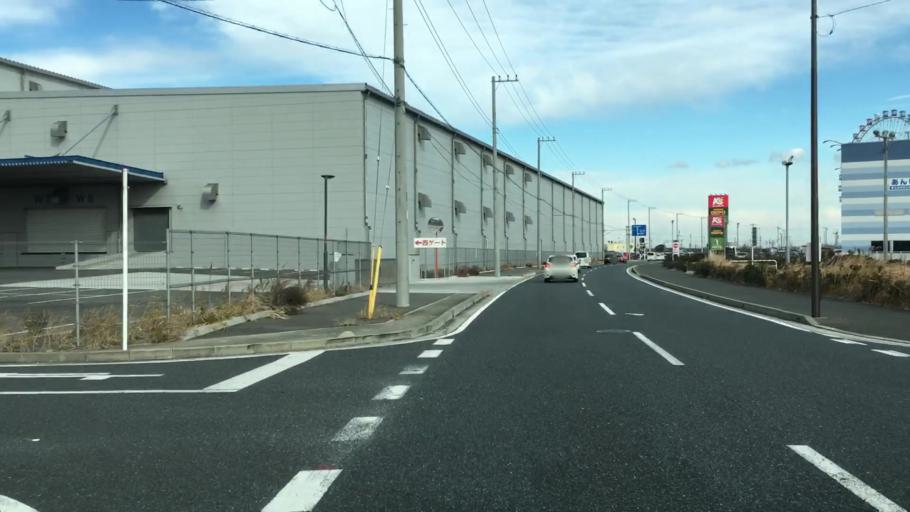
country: JP
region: Chiba
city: Kisarazu
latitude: 35.4385
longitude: 139.9284
